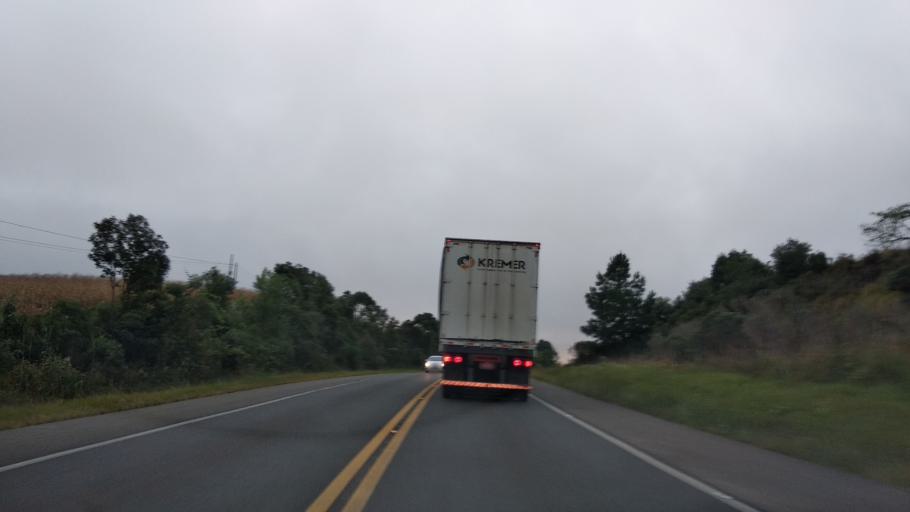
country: BR
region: Santa Catarina
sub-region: Campos Novos
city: Campos Novos
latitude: -27.3753
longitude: -51.0852
